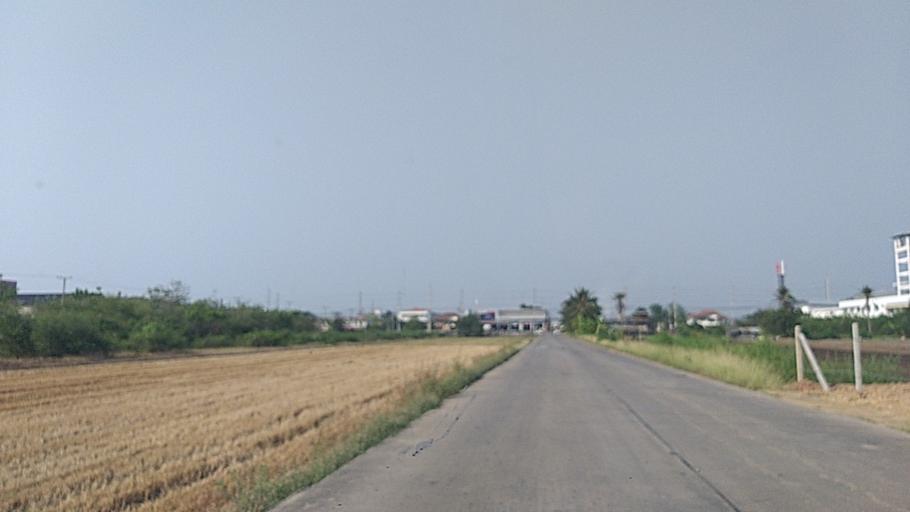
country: TH
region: Nonthaburi
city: Sai Noi
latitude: 13.9796
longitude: 100.3222
